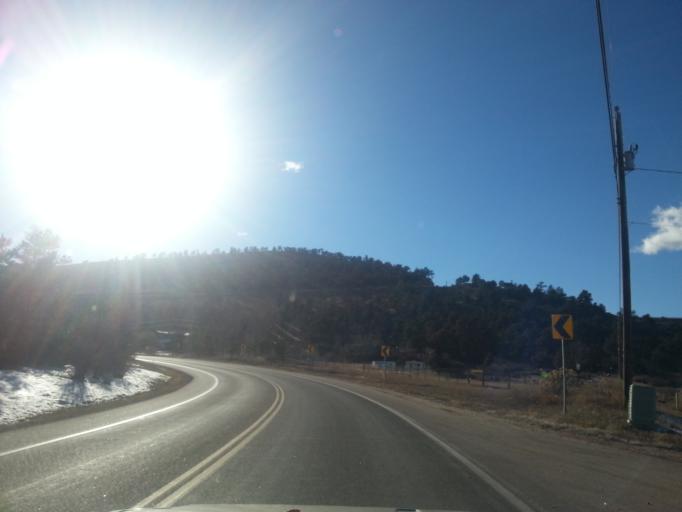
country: US
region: Colorado
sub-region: Larimer County
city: Fort Collins
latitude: 40.5302
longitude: -105.1335
